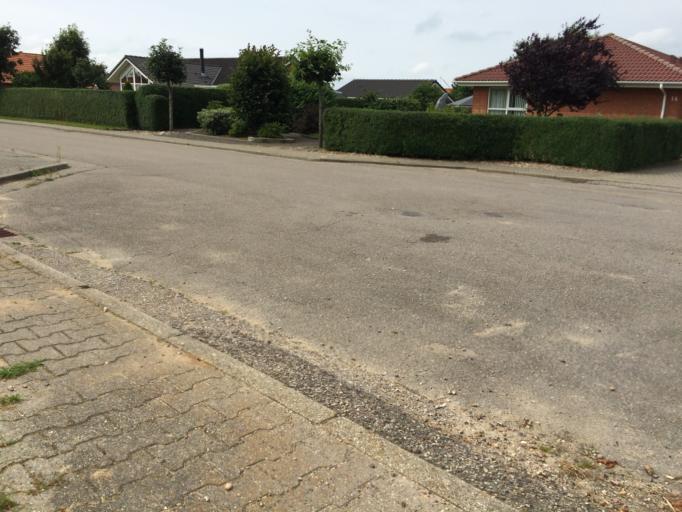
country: DK
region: Central Jutland
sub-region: Holstebro Kommune
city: Ulfborg
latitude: 56.2746
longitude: 8.3095
